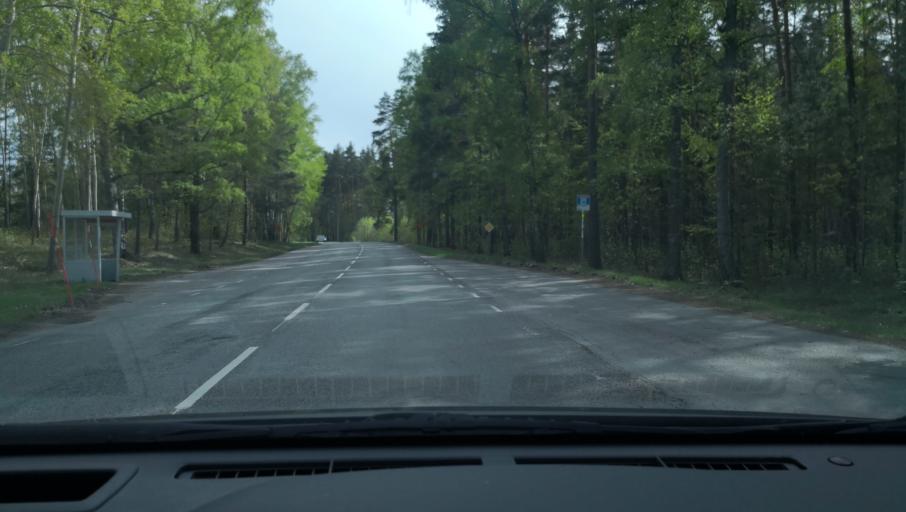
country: SE
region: OErebro
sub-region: Kumla Kommun
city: Kumla
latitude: 59.0921
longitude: 15.1582
